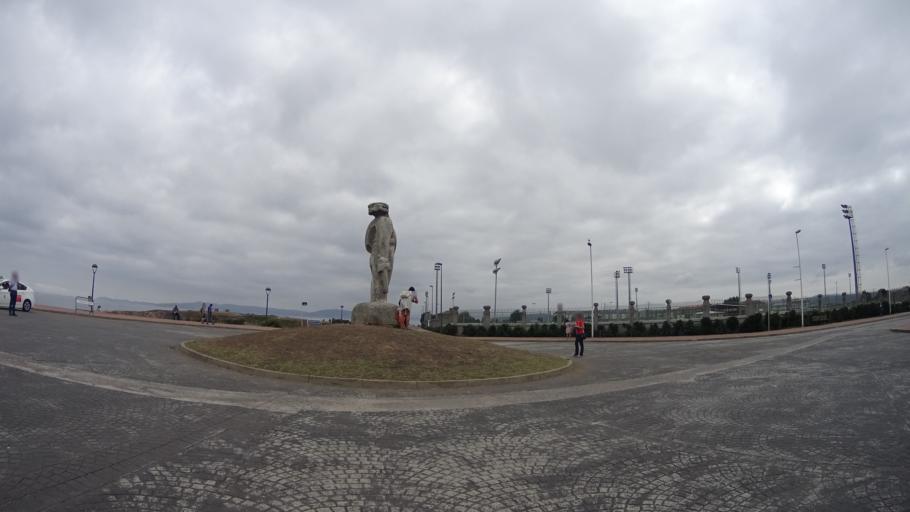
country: ES
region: Galicia
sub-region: Provincia da Coruna
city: A Coruna
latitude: 43.3848
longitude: -8.4027
